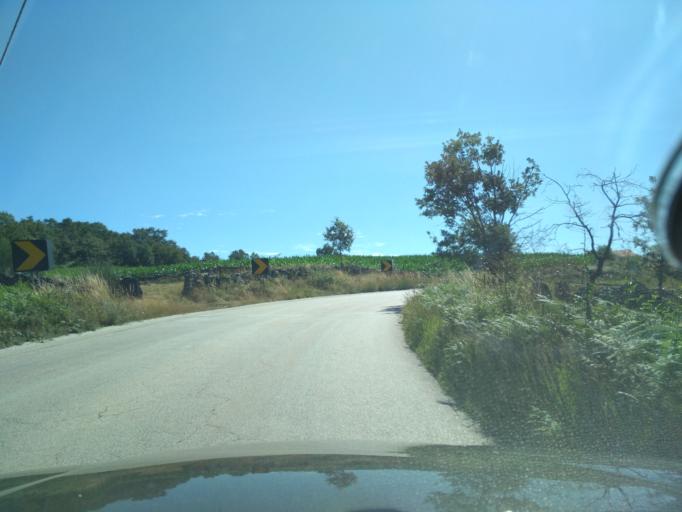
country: PT
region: Vila Real
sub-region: Ribeira de Pena
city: Ribeira de Pena
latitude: 41.5008
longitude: -7.7483
